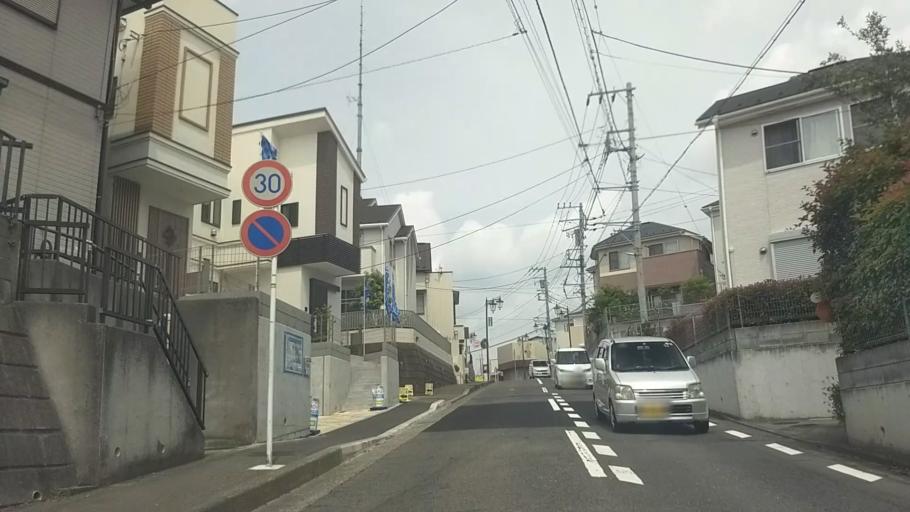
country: JP
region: Kanagawa
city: Fujisawa
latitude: 35.3653
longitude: 139.4689
